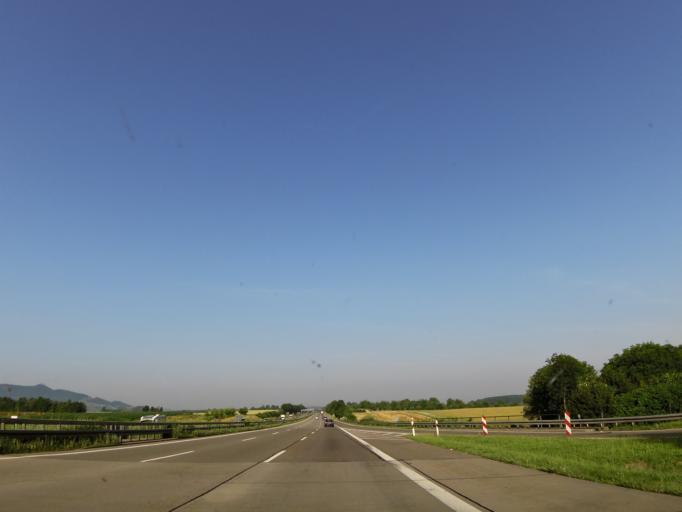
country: DE
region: Baden-Wuerttemberg
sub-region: Regierungsbezirk Stuttgart
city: Weilheim an der Teck
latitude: 48.6317
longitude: 9.5364
